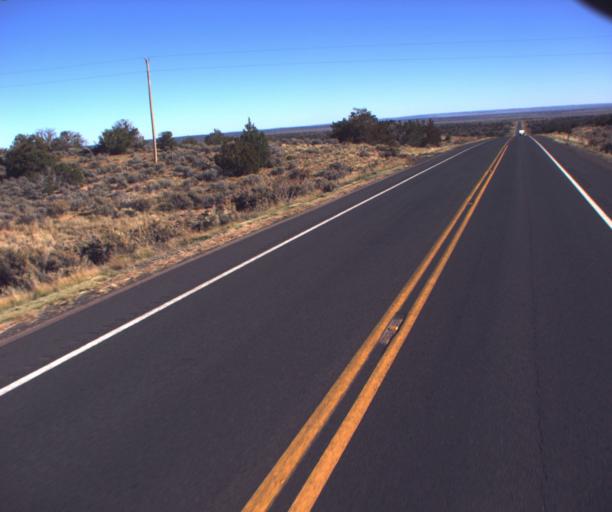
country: US
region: Arizona
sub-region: Apache County
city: Houck
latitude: 35.3465
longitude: -109.4529
